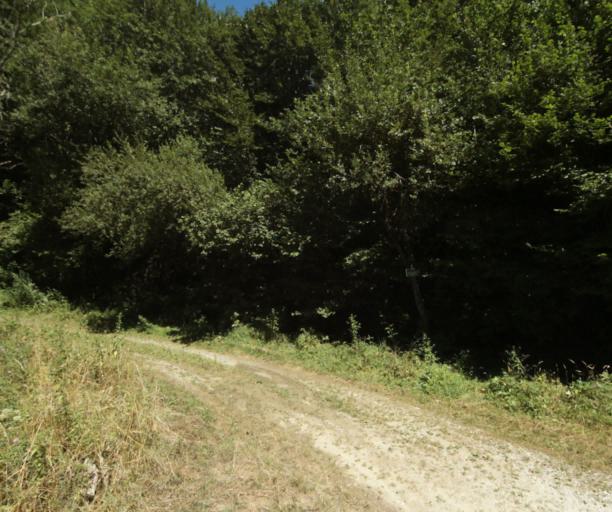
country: FR
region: Midi-Pyrenees
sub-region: Departement du Tarn
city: Soreze
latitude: 43.4384
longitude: 2.1036
